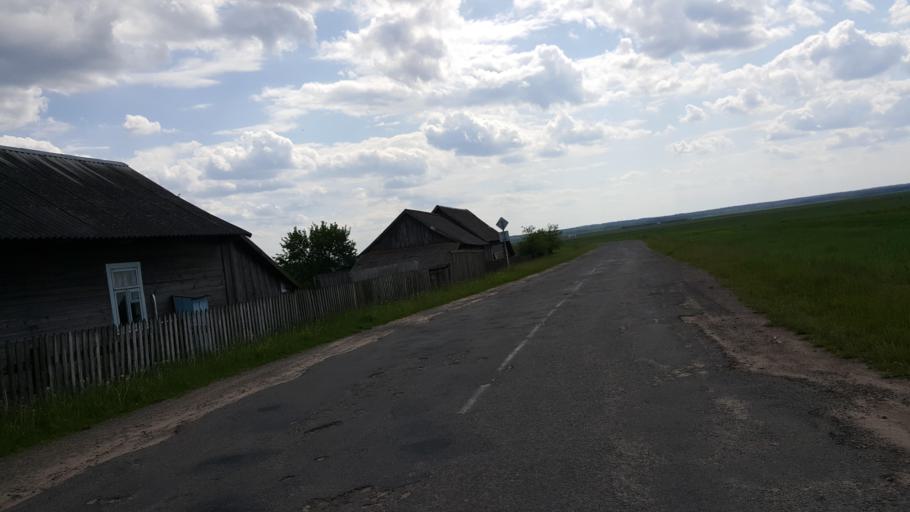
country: PL
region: Podlasie
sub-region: Powiat hajnowski
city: Bialowieza
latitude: 52.6609
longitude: 24.0878
